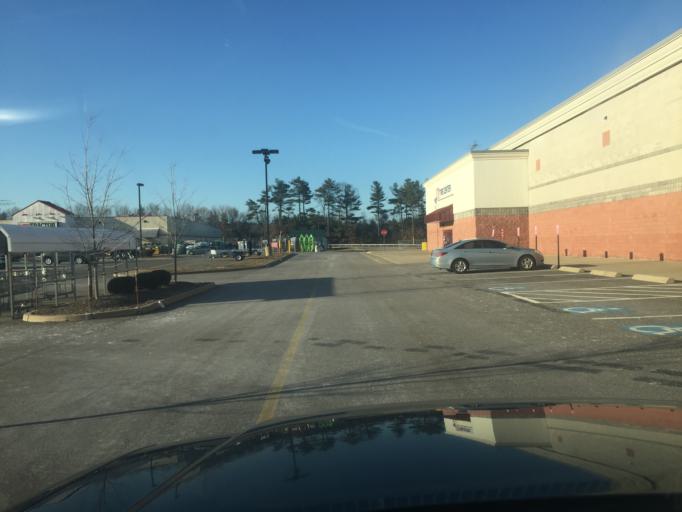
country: US
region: Massachusetts
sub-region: Bristol County
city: Raynham
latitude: 41.9599
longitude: -71.1169
